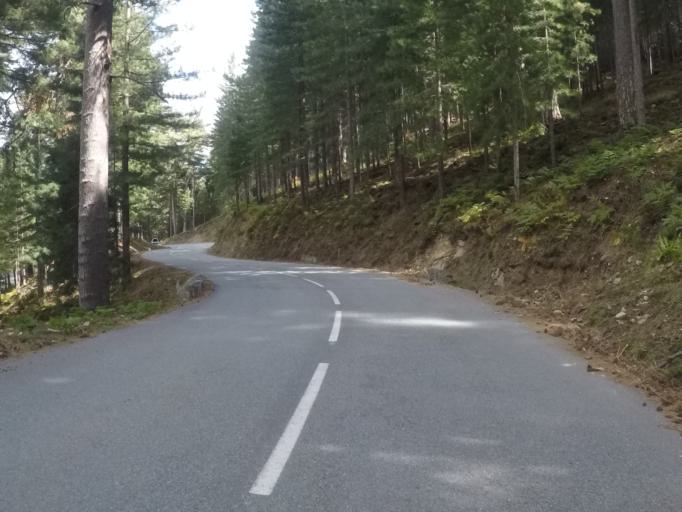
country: FR
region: Corsica
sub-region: Departement de la Corse-du-Sud
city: Zonza
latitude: 41.8032
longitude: 9.2392
